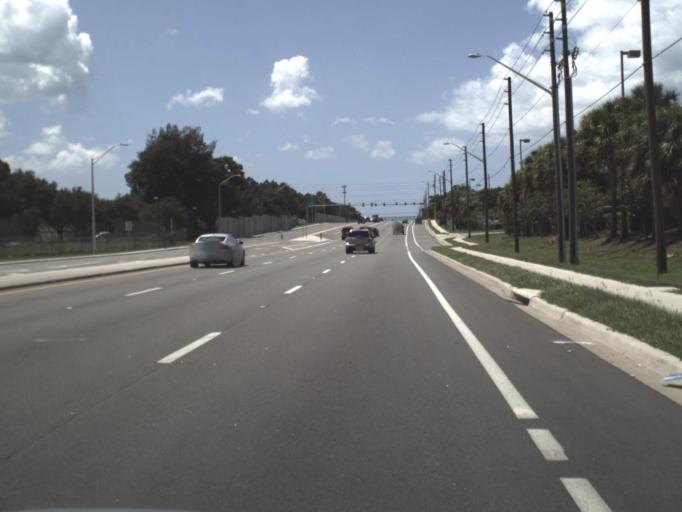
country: US
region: Florida
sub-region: Pinellas County
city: Ridgecrest
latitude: 27.8948
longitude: -82.7916
